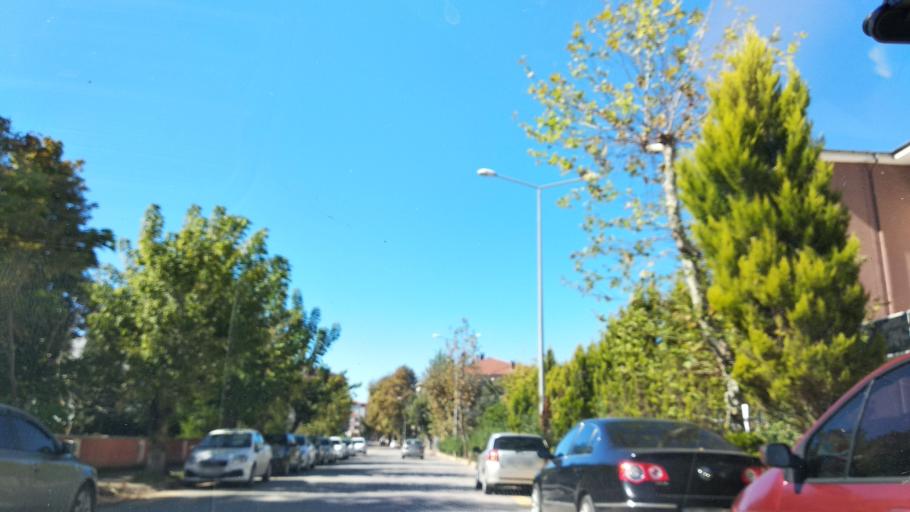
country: TR
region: Sakarya
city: Karasu
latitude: 41.0913
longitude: 30.6992
